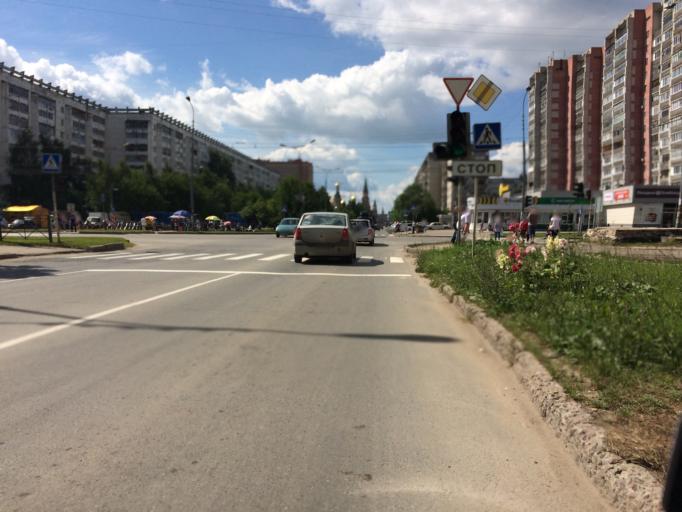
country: RU
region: Mariy-El
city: Yoshkar-Ola
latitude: 56.6307
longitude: 47.9189
